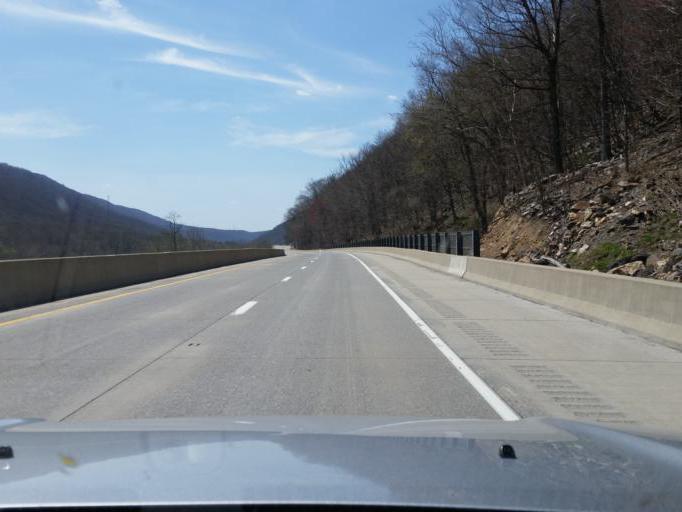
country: US
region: Pennsylvania
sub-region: Mifflin County
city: Highland Park
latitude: 40.6012
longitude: -77.4889
